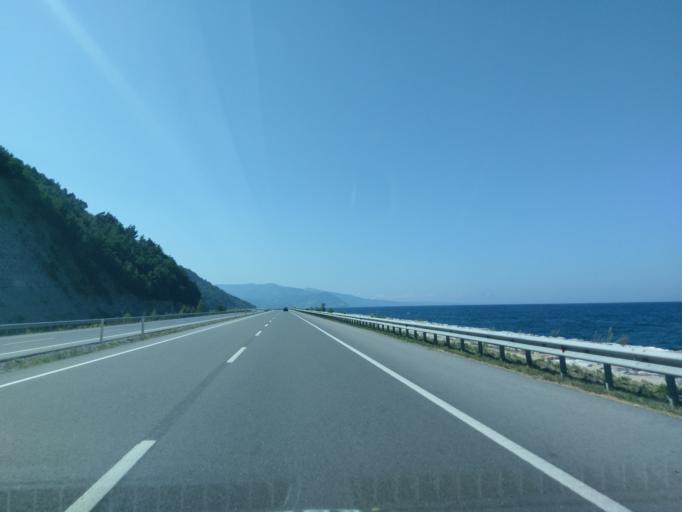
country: TR
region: Sinop
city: Dikmen
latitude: 41.6914
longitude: 35.3686
